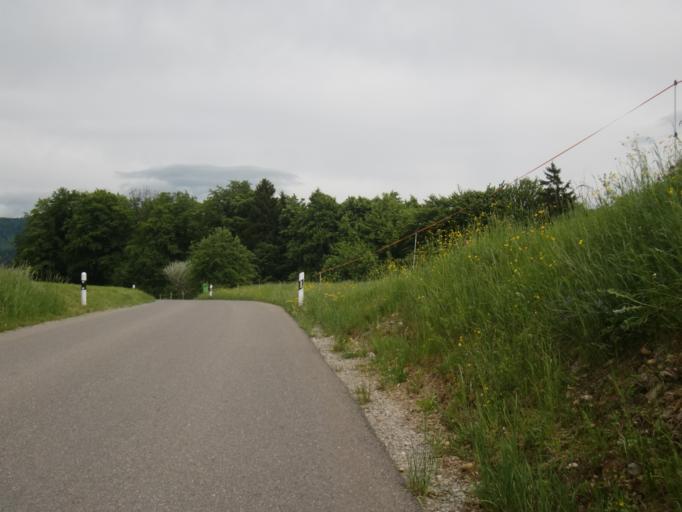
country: CH
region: Zurich
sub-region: Bezirk Hinwil
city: Wald
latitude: 47.2812
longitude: 8.9049
